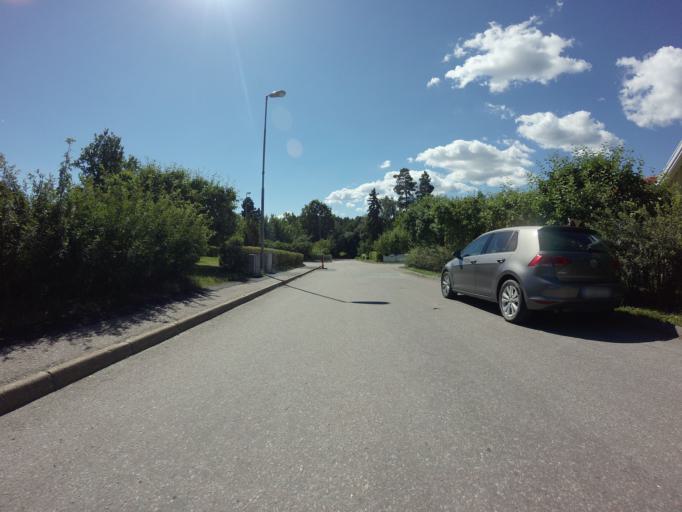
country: SE
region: Stockholm
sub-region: Sollentuna Kommun
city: Sollentuna
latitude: 59.4514
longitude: 17.8952
